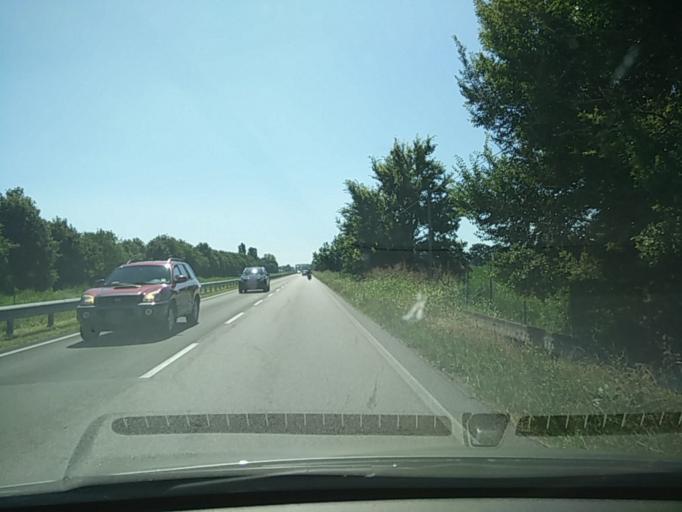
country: IT
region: Veneto
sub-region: Provincia di Venezia
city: San Giorgio di Livenza
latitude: 45.6255
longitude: 12.7883
